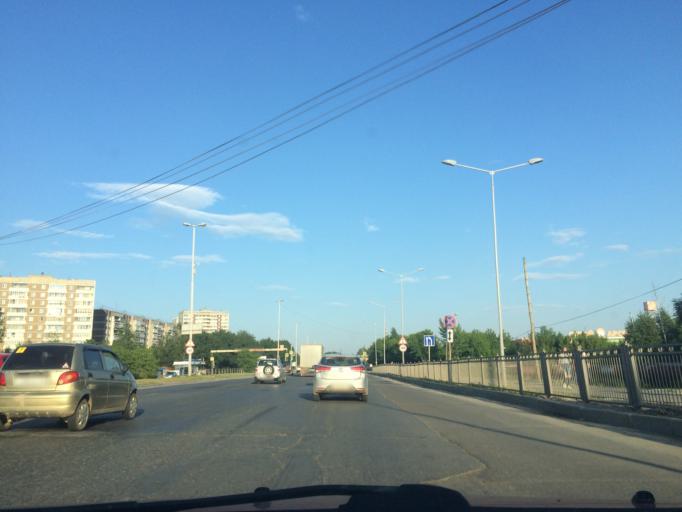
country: RU
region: Sverdlovsk
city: Yekaterinburg
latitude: 56.8282
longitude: 60.6802
